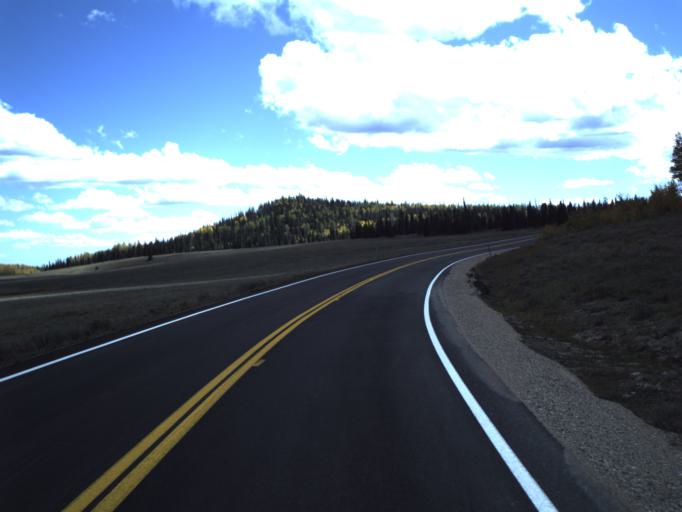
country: US
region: Utah
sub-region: Iron County
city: Parowan
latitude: 37.5661
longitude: -112.7896
